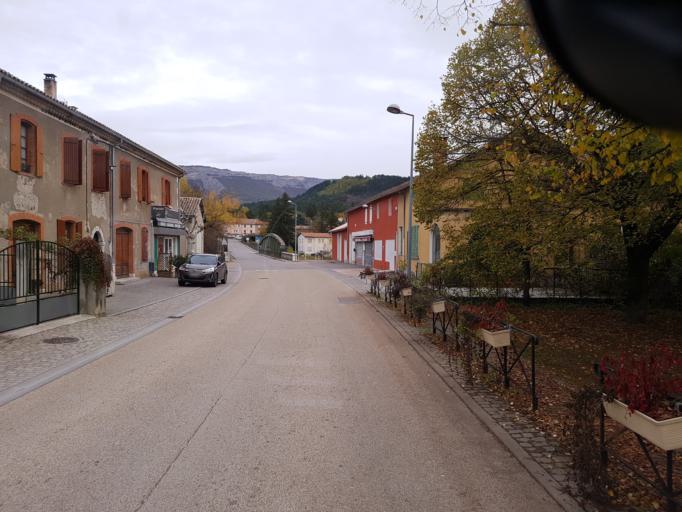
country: FR
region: Provence-Alpes-Cote d'Azur
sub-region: Departement des Hautes-Alpes
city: Laragne-Monteglin
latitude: 44.3439
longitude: 5.7691
